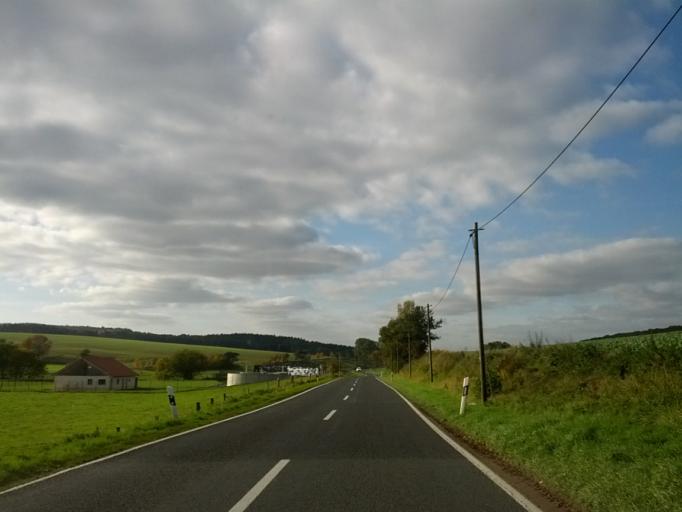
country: DE
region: Thuringia
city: Marksuhl
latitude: 50.9156
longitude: 10.1919
